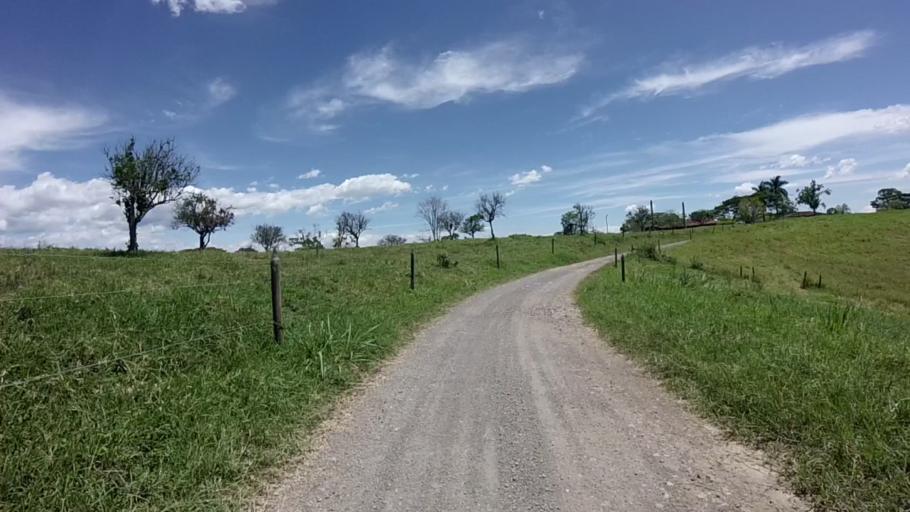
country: CO
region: Valle del Cauca
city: Alcala
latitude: 4.7124
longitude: -75.8015
